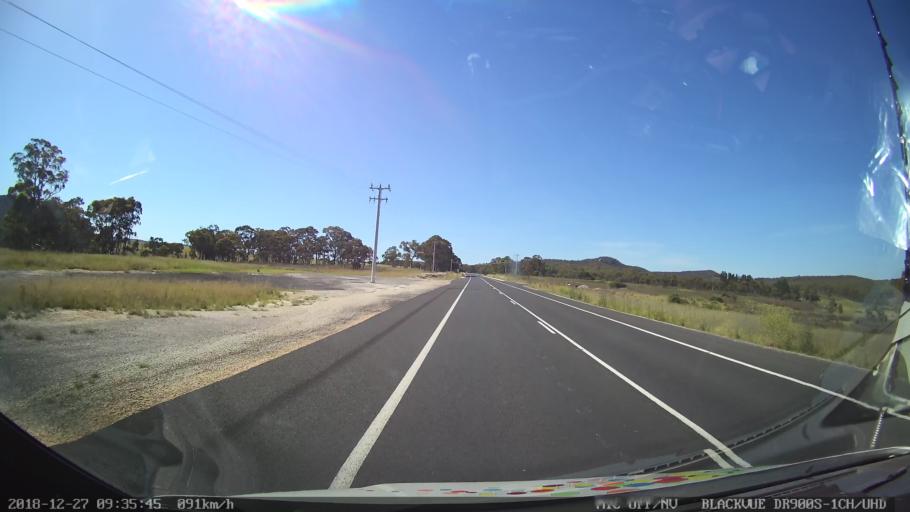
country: AU
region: New South Wales
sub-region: Lithgow
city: Portland
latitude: -33.2428
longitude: 150.0321
